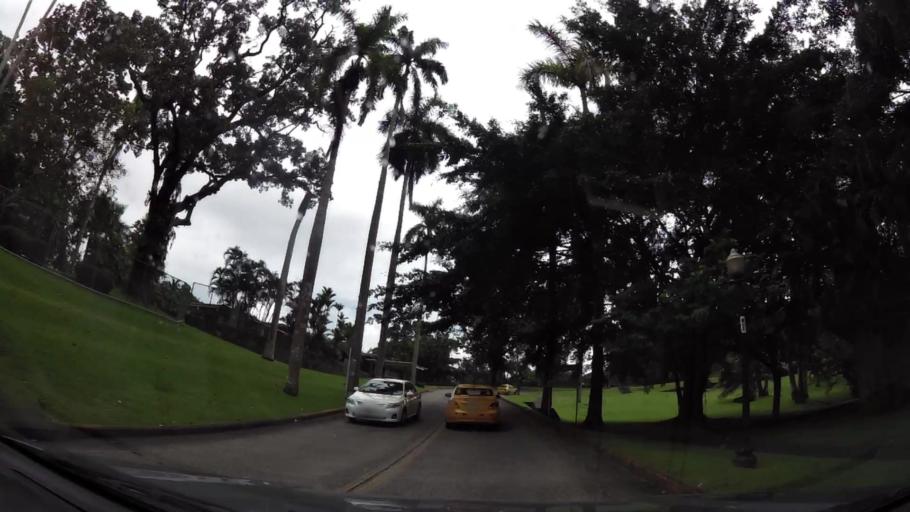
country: PA
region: Panama
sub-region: Distrito de Panama
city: Ancon
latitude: 8.9598
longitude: -79.5527
